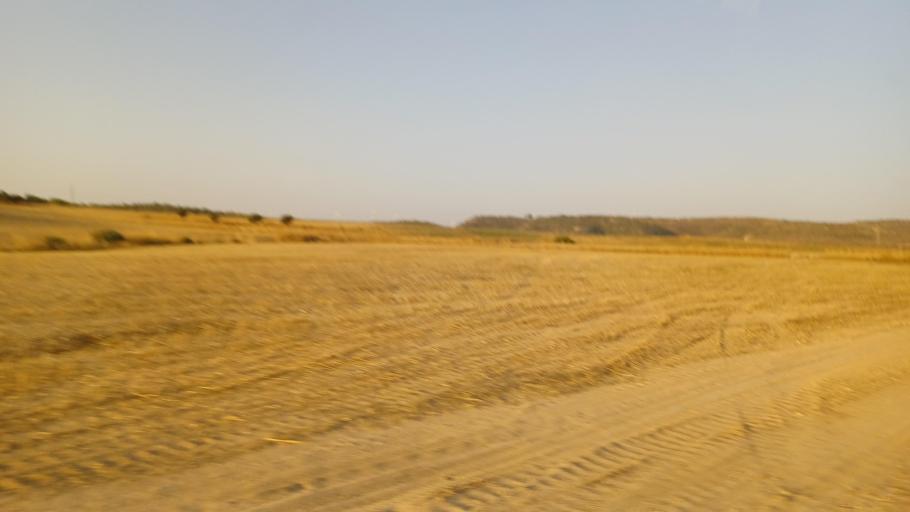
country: CY
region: Lefkosia
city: Lympia
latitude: 34.9976
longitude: 33.5148
